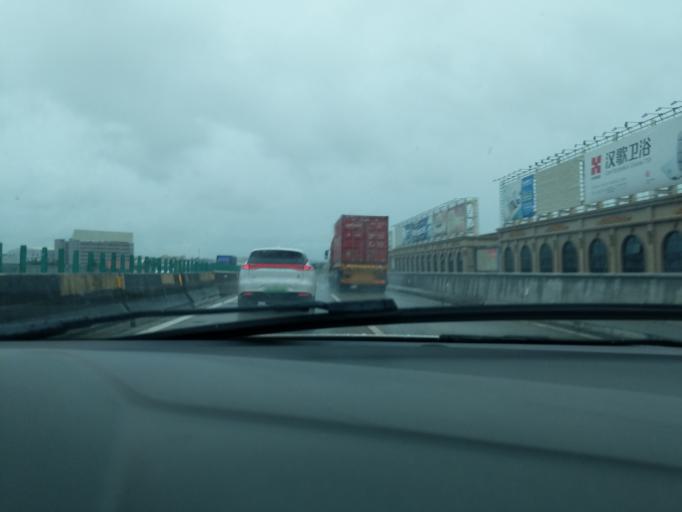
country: CN
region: Guangdong
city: Shuikou
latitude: 22.4772
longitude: 112.7679
